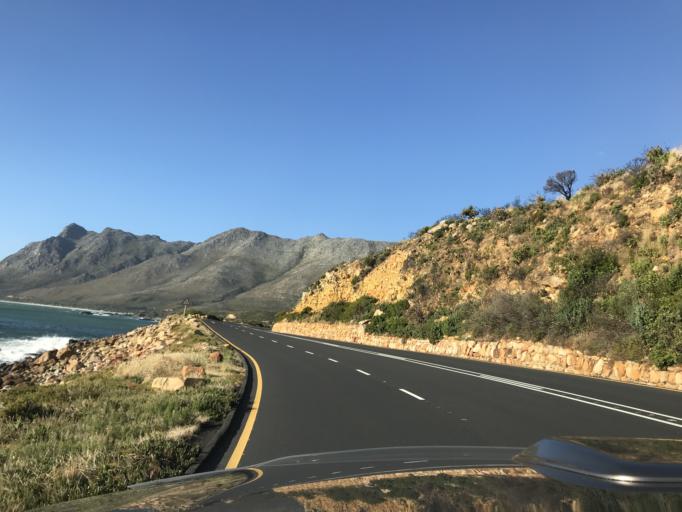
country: ZA
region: Western Cape
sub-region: Overberg District Municipality
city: Grabouw
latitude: -34.2576
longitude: 18.8545
